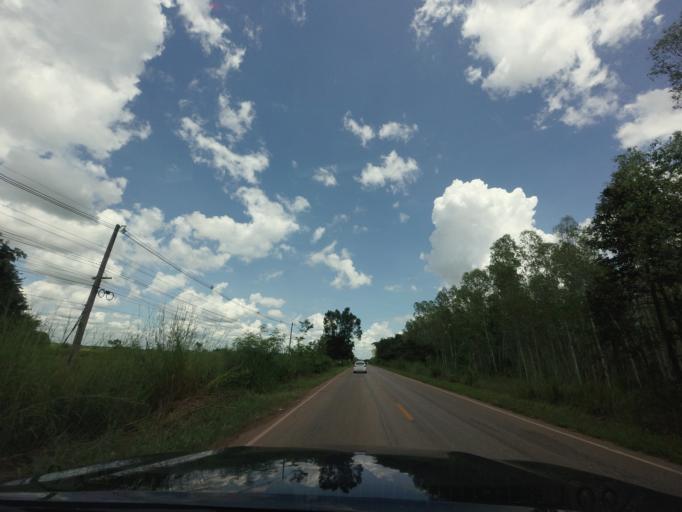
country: TH
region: Changwat Udon Thani
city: Ban Dung
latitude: 17.6826
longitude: 103.1915
